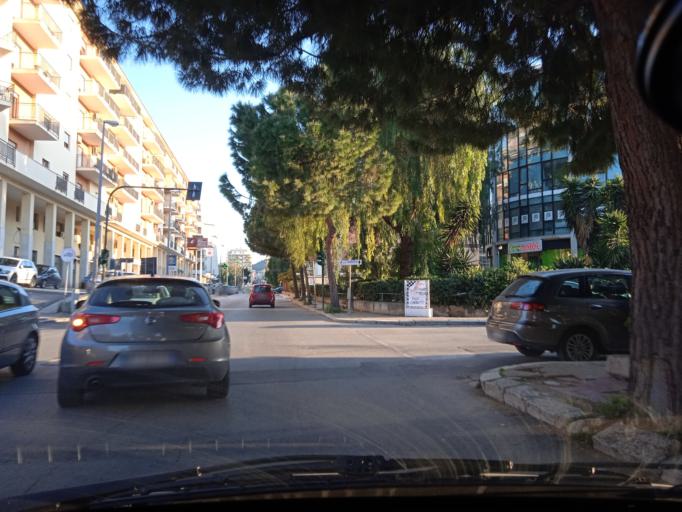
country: IT
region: Sicily
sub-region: Palermo
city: Bagheria
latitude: 38.0841
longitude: 13.5013
